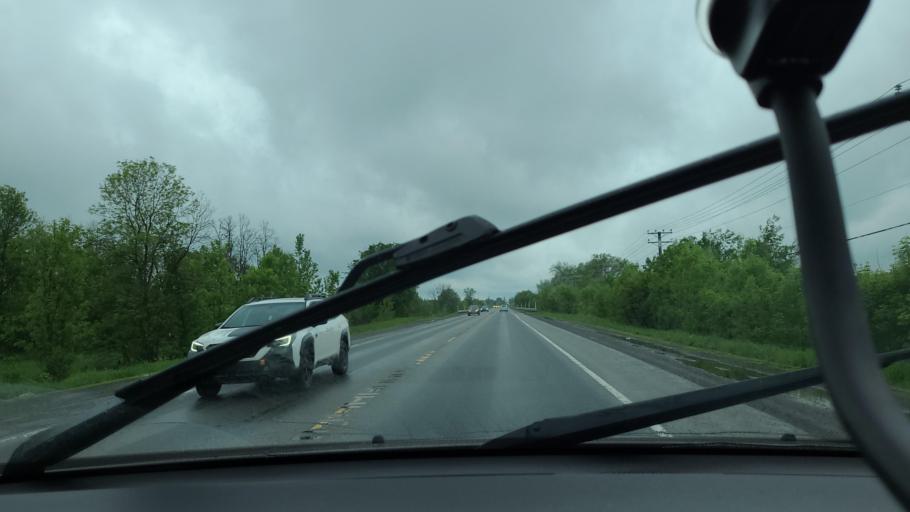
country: CA
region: Quebec
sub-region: Laurentides
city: Saint-Jerome
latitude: 45.7412
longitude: -74.0303
